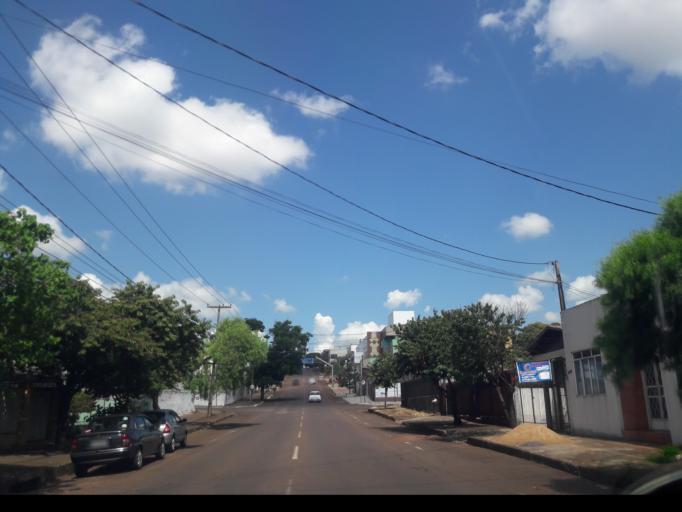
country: BR
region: Parana
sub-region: Cascavel
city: Cascavel
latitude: -24.9648
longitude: -53.4604
